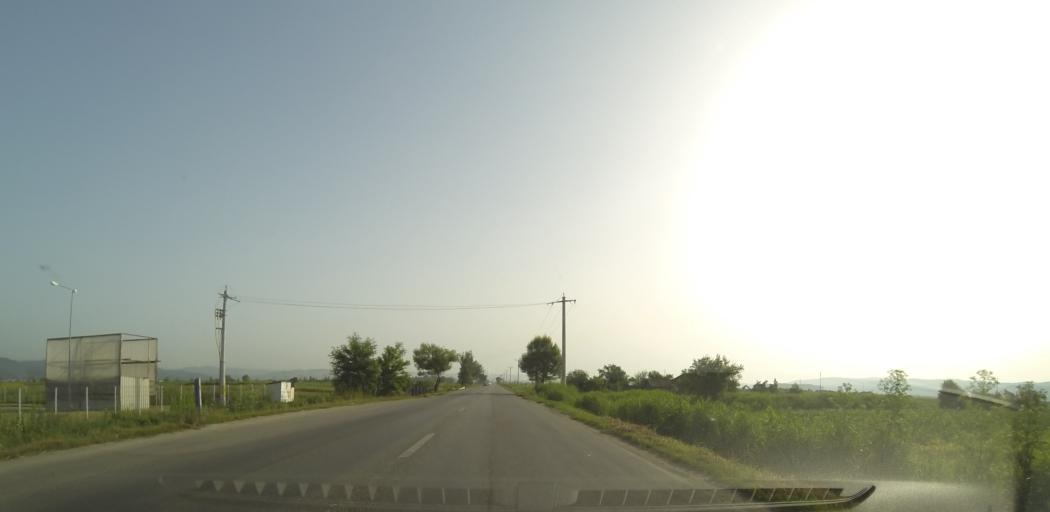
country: RO
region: Valcea
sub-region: Comuna Mihaesti
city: Mihaesti
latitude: 44.9973
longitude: 24.2602
